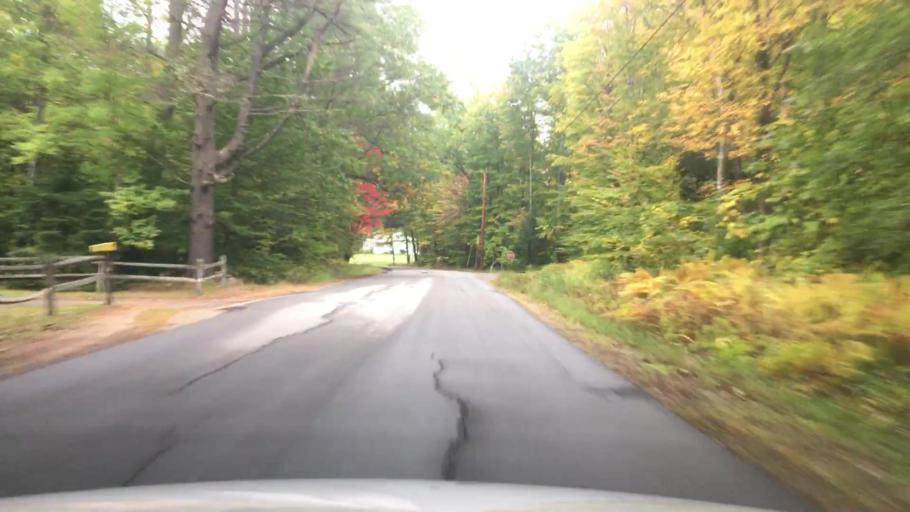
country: US
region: Maine
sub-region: Oxford County
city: Bethel
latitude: 44.4829
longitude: -70.7611
